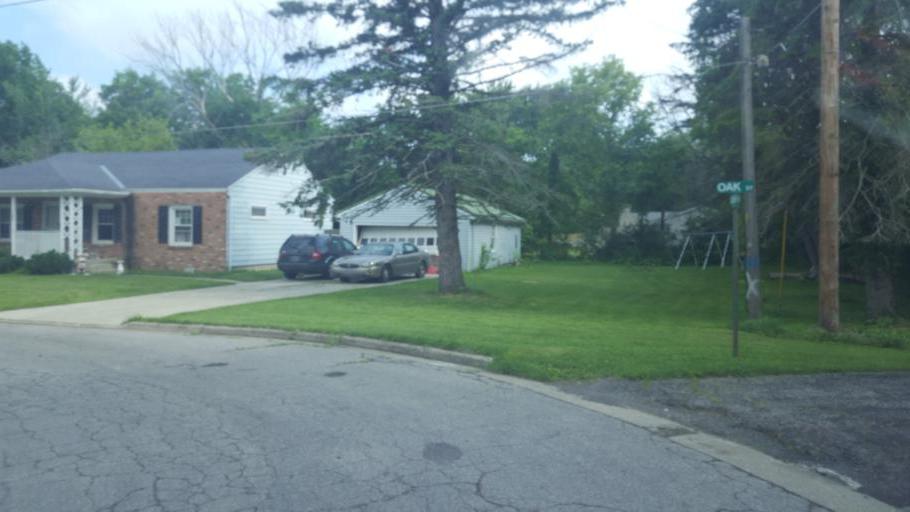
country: US
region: Ohio
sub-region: Crawford County
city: Galion
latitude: 40.7225
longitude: -82.7849
